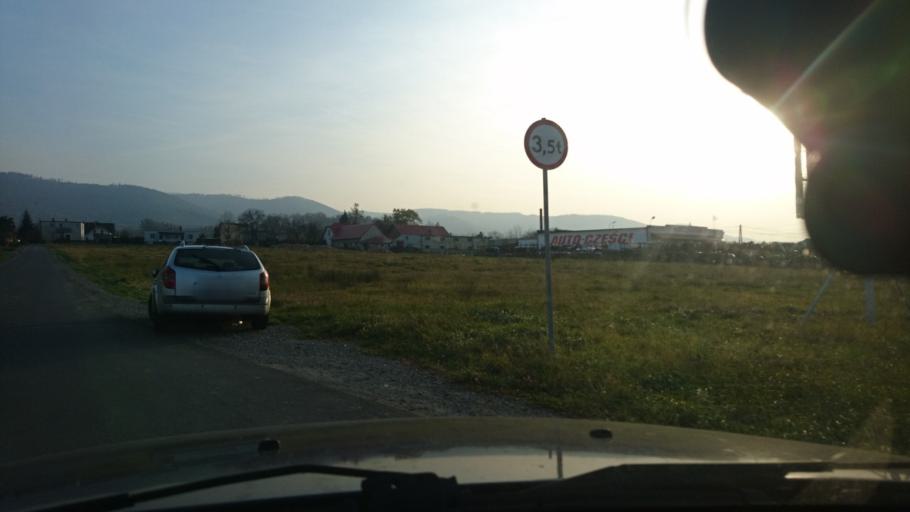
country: PL
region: Silesian Voivodeship
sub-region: Powiat bielski
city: Jaworze
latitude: 49.8059
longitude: 18.9524
